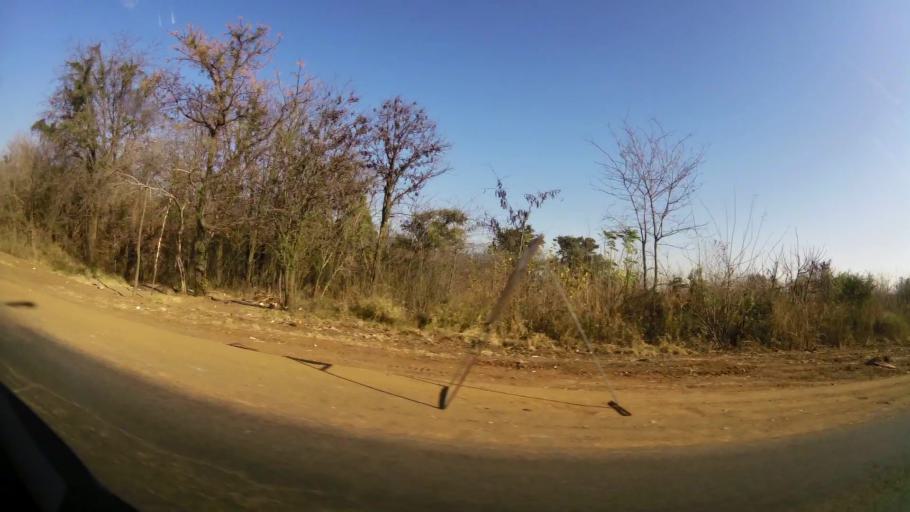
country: ZA
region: Gauteng
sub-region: City of Tshwane Metropolitan Municipality
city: Pretoria
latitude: -25.6395
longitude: 28.1980
